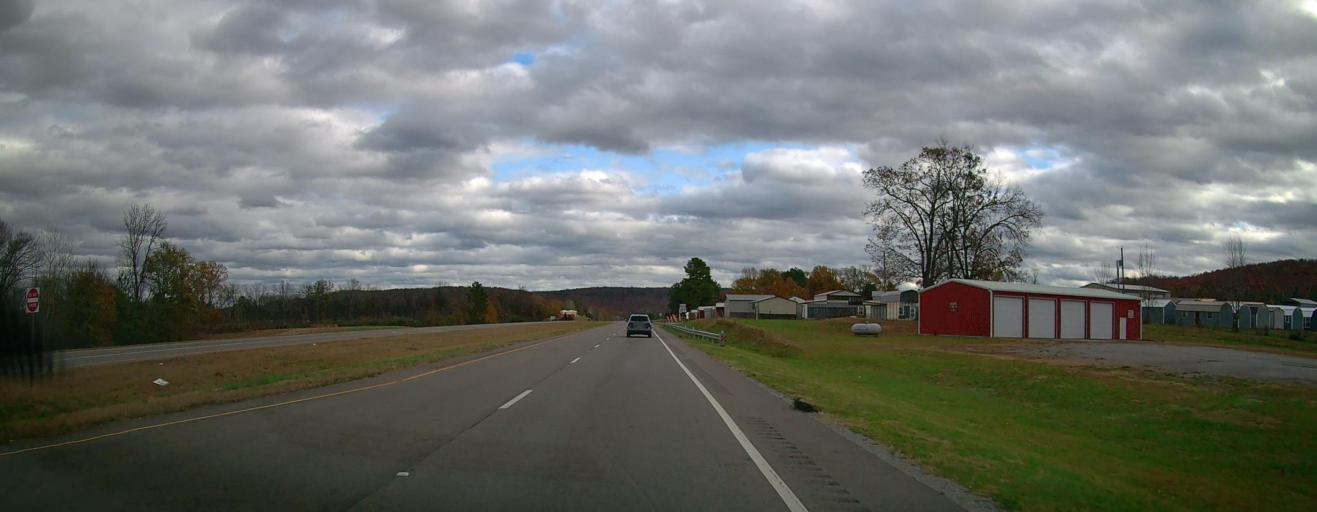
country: US
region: Alabama
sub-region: Morgan County
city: Danville
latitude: 34.3384
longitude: -87.0223
